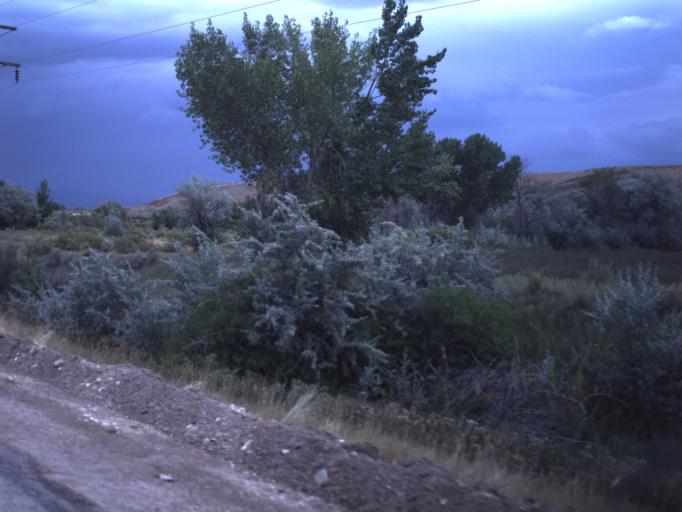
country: US
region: Utah
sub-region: Duchesne County
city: Roosevelt
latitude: 40.3395
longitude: -110.0244
